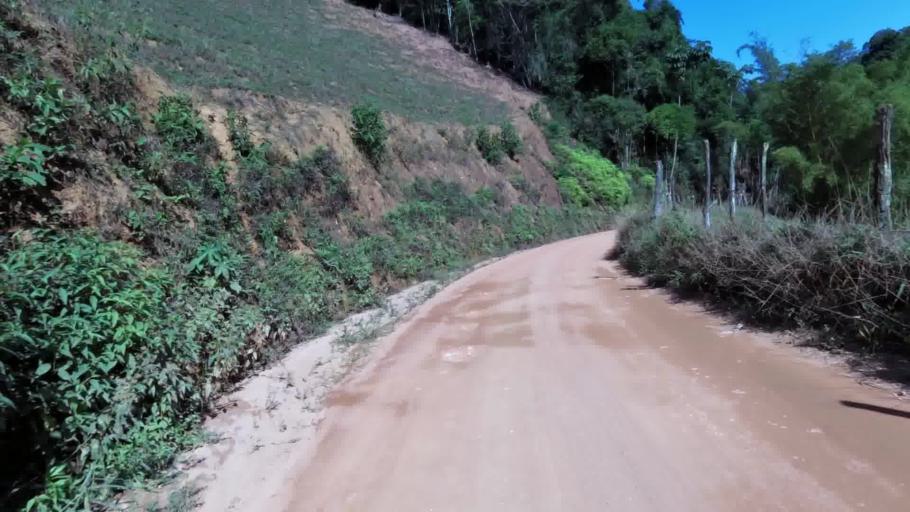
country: BR
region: Espirito Santo
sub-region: Alfredo Chaves
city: Alfredo Chaves
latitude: -20.5761
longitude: -40.7917
